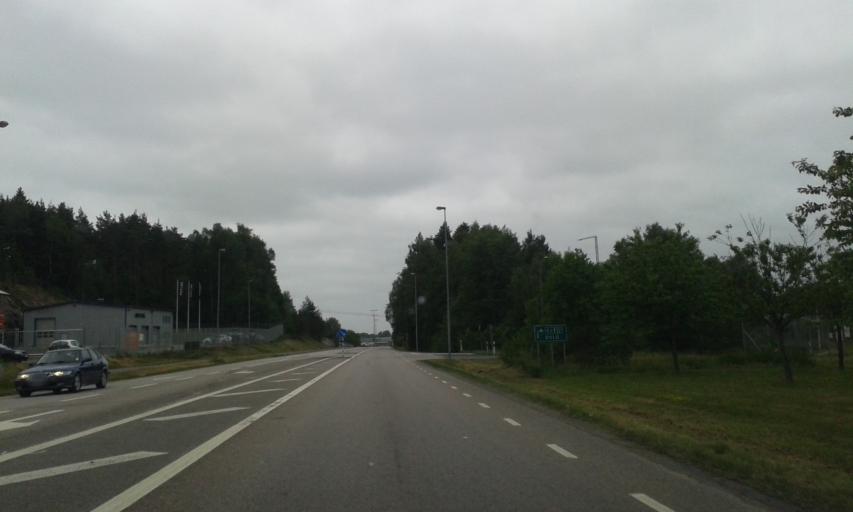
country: SE
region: Vaestra Goetaland
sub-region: Kungalvs Kommun
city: Kungalv
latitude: 57.8867
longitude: 11.9473
